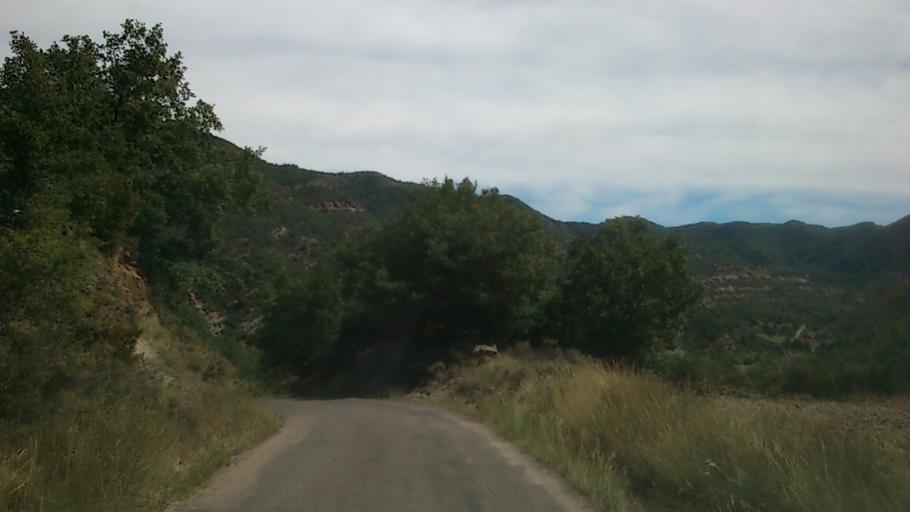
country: ES
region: Aragon
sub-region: Provincia de Huesca
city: Arguis
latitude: 42.3104
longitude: -0.3521
